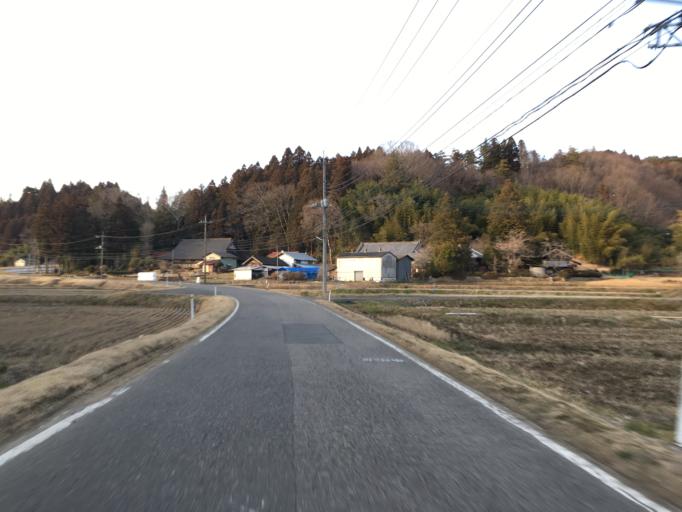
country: JP
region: Ibaraki
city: Daigo
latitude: 36.7948
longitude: 140.4111
